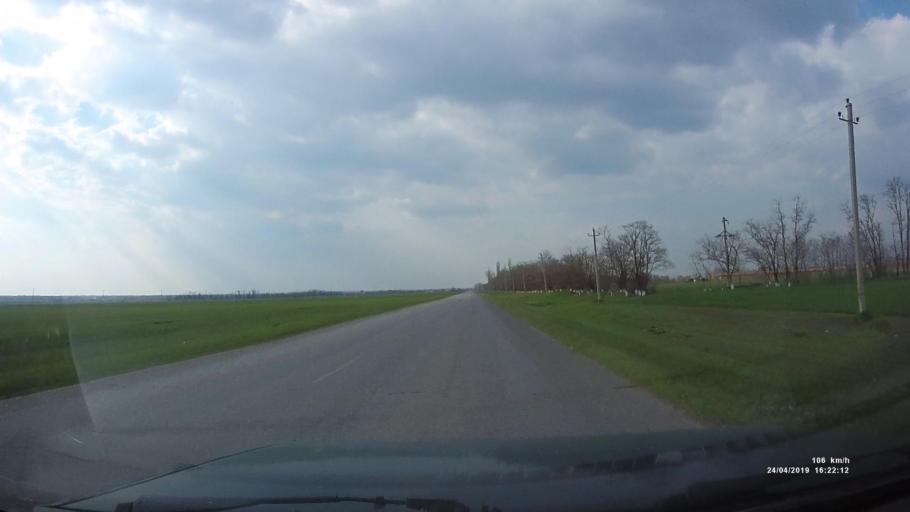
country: RU
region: Rostov
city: Orlovskiy
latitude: 46.8161
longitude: 42.0582
